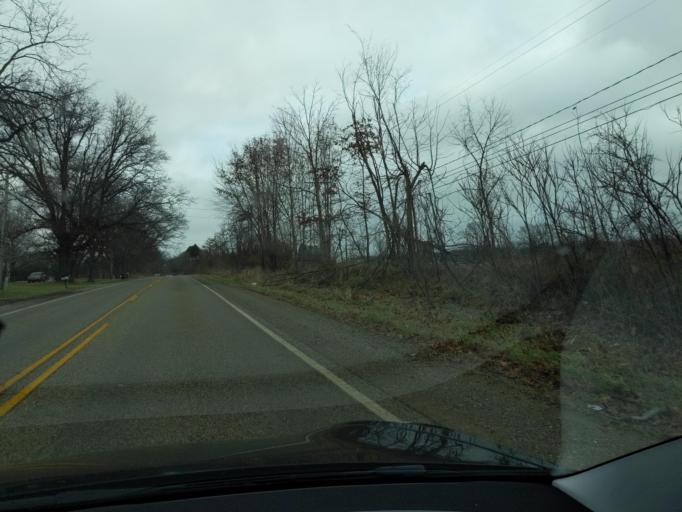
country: US
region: Michigan
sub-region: Jackson County
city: Spring Arbor
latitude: 42.2524
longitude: -84.5334
